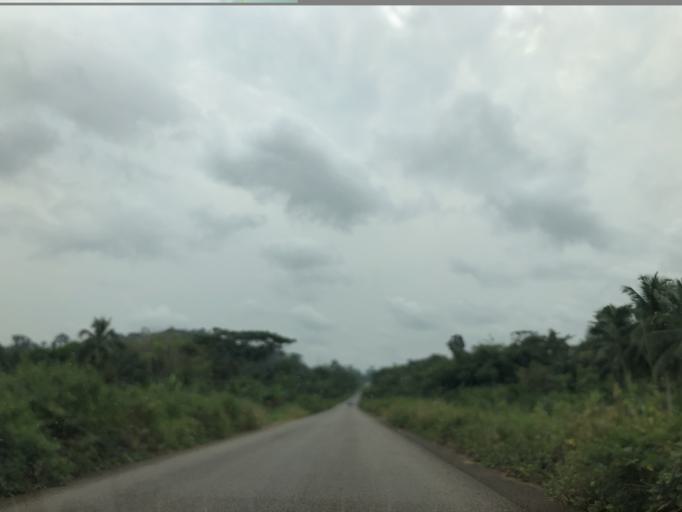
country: CM
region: Littoral
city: Edea
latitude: 3.6361
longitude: 10.1155
